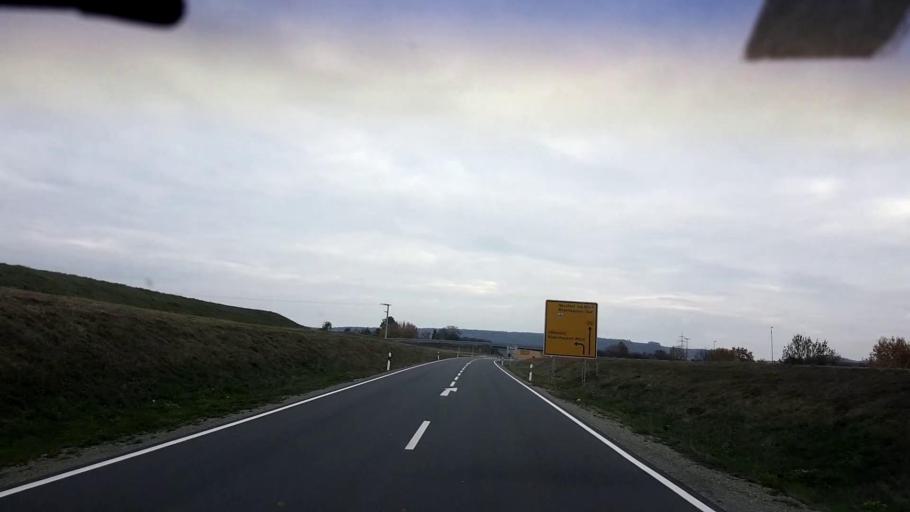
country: DE
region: Bavaria
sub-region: Regierungsbezirk Unterfranken
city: Castell
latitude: 49.7672
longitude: 10.3479
